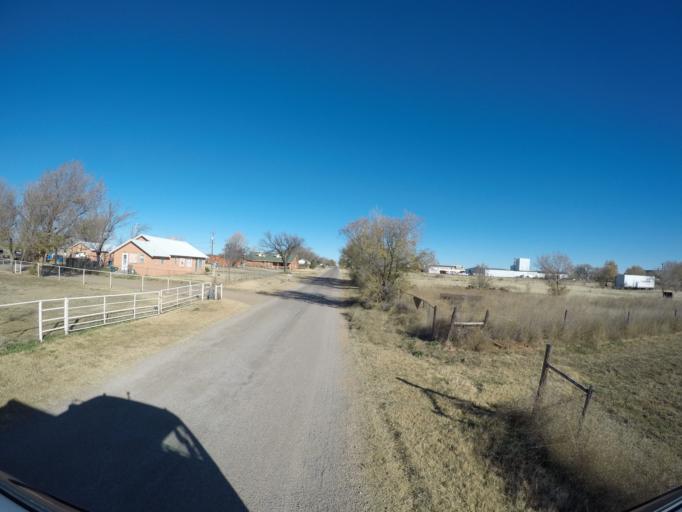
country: US
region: New Mexico
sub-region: Curry County
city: Clovis
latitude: 34.4417
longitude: -103.1996
